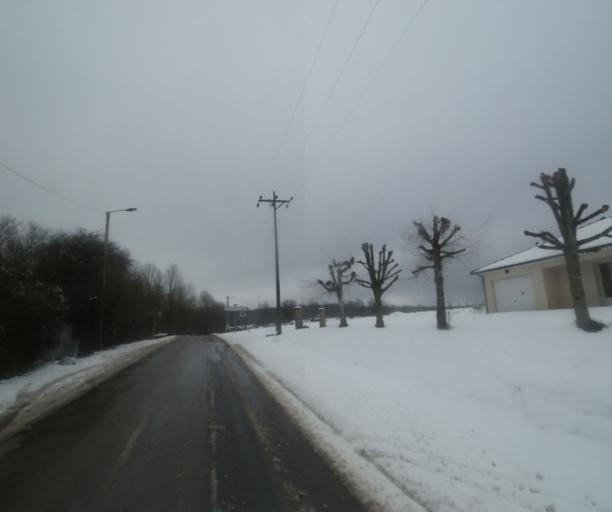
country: FR
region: Champagne-Ardenne
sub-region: Departement de la Haute-Marne
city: Laneuville-a-Remy
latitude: 48.4726
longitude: 4.8839
